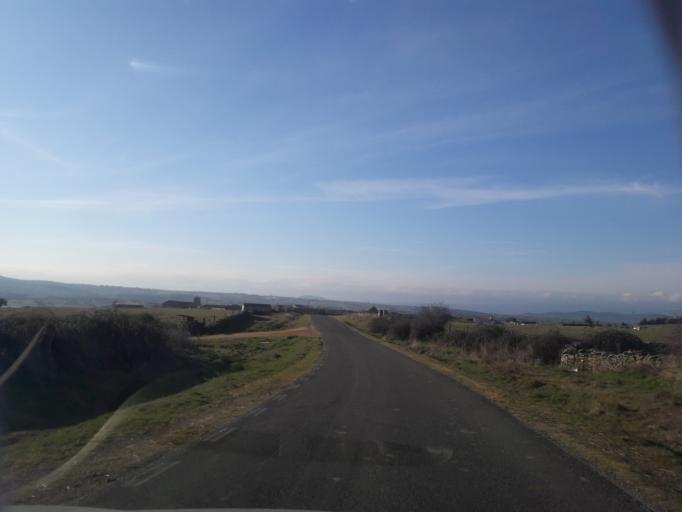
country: ES
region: Castille and Leon
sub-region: Provincia de Salamanca
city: Salvatierra de Tormes
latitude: 40.5942
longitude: -5.5993
